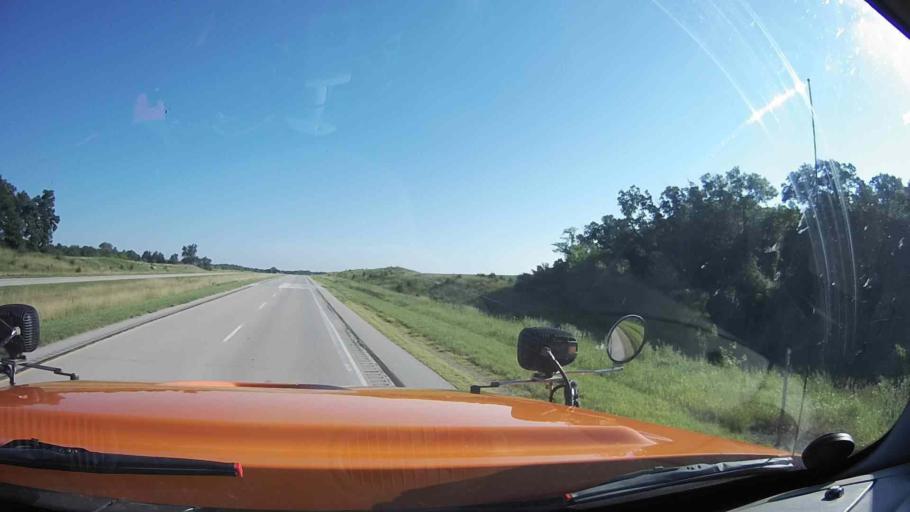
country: US
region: Iowa
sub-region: Lee County
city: Fort Madison
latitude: 40.6590
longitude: -91.3609
